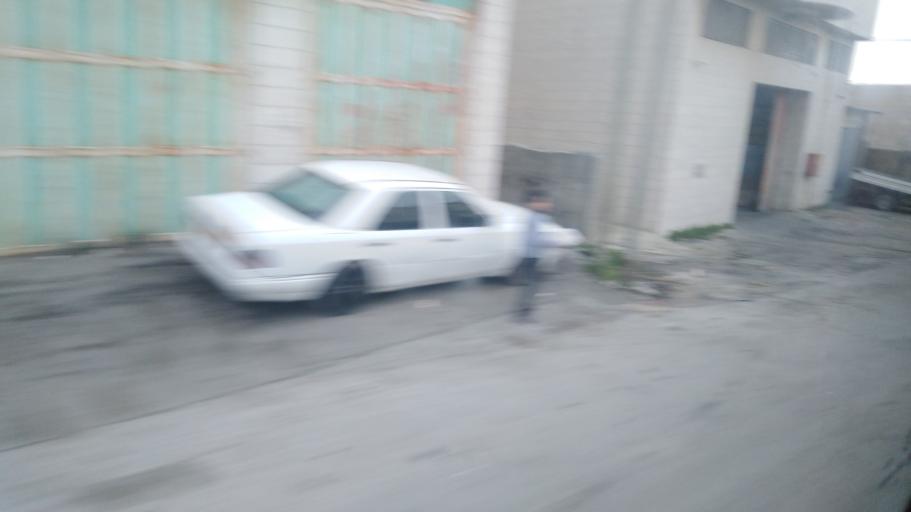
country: PS
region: West Bank
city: Hebron
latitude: 31.5242
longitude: 35.0757
